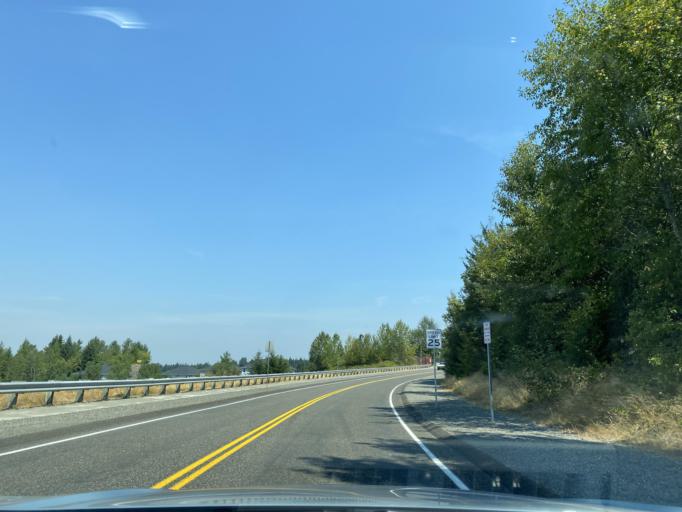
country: US
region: Washington
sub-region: Pierce County
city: Bonney Lake
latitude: 47.1673
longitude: -122.1916
